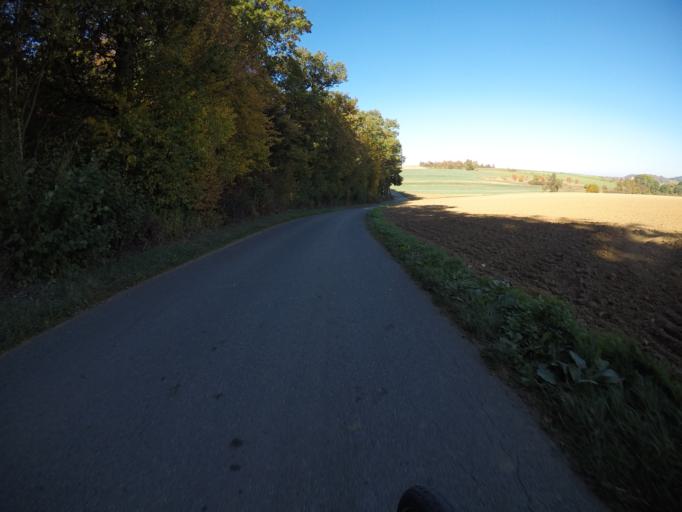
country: DE
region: Baden-Wuerttemberg
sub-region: Regierungsbezirk Stuttgart
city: Herrenberg
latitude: 48.5712
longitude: 8.8439
